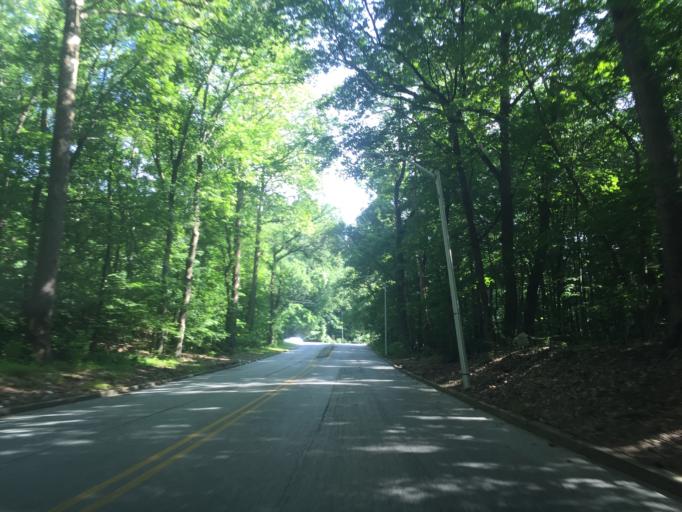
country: US
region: Maryland
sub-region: Baltimore County
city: Lochearn
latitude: 39.3561
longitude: -76.6549
